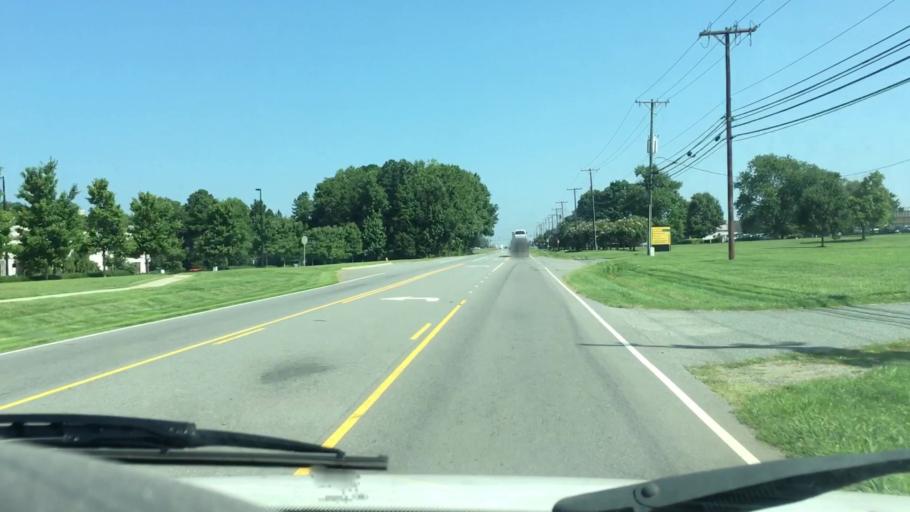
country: US
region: North Carolina
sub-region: Mecklenburg County
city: Huntersville
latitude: 35.3408
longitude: -80.8421
